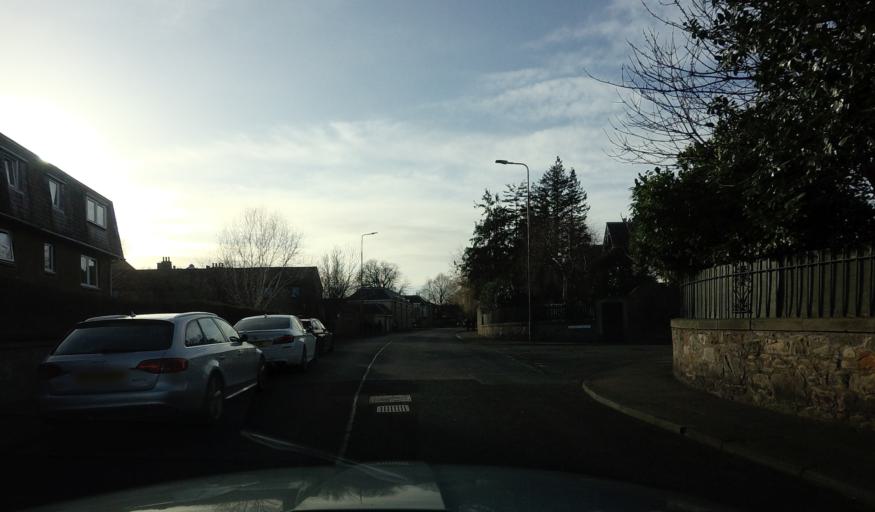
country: GB
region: Scotland
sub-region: Edinburgh
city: Edinburgh
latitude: 55.9756
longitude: -3.2042
